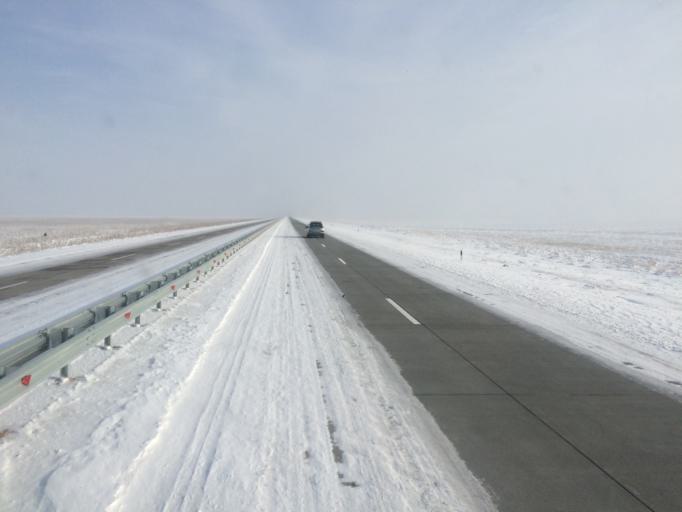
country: KZ
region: Zhambyl
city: Georgiyevka
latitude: 43.3447
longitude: 74.3396
